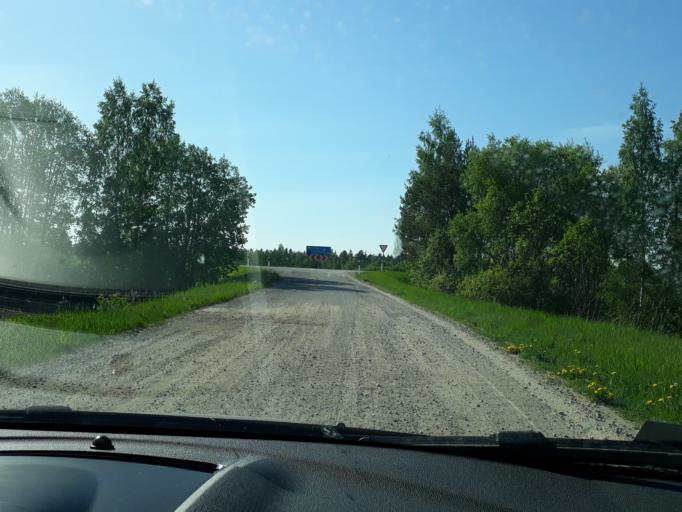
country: EE
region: Paernumaa
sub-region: Tootsi vald
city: Tootsi
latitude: 58.5841
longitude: 24.8978
